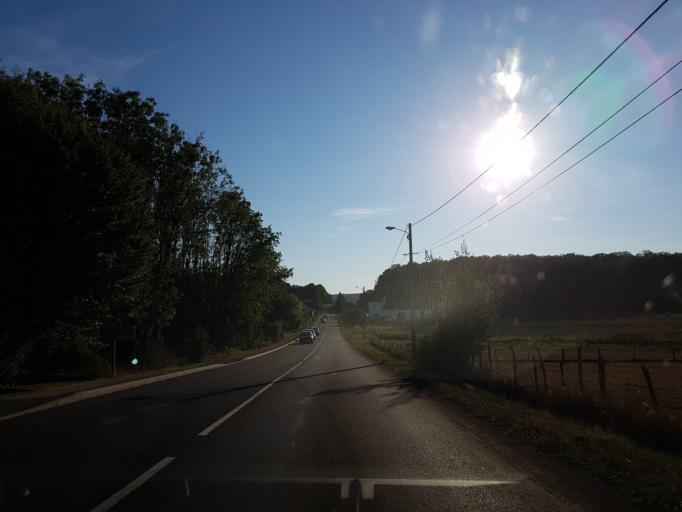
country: FR
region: Franche-Comte
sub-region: Departement de la Haute-Saone
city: Magny-Vernois
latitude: 47.6778
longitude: 6.4087
